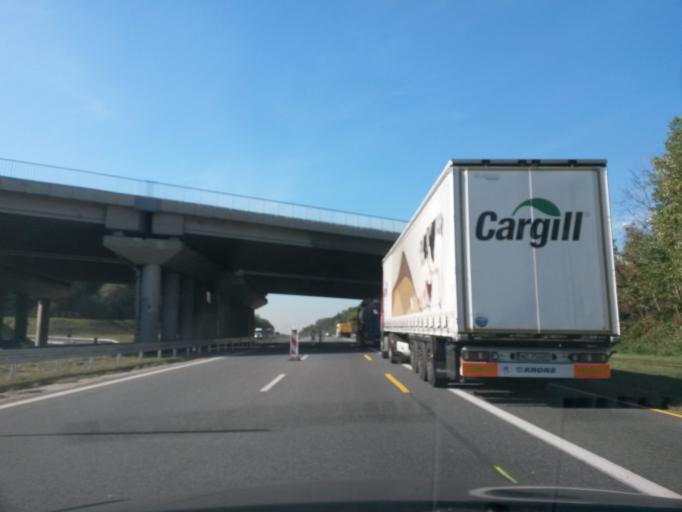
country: PL
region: Silesian Voivodeship
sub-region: Myslowice
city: Myslowice
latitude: 50.2163
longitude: 19.1291
